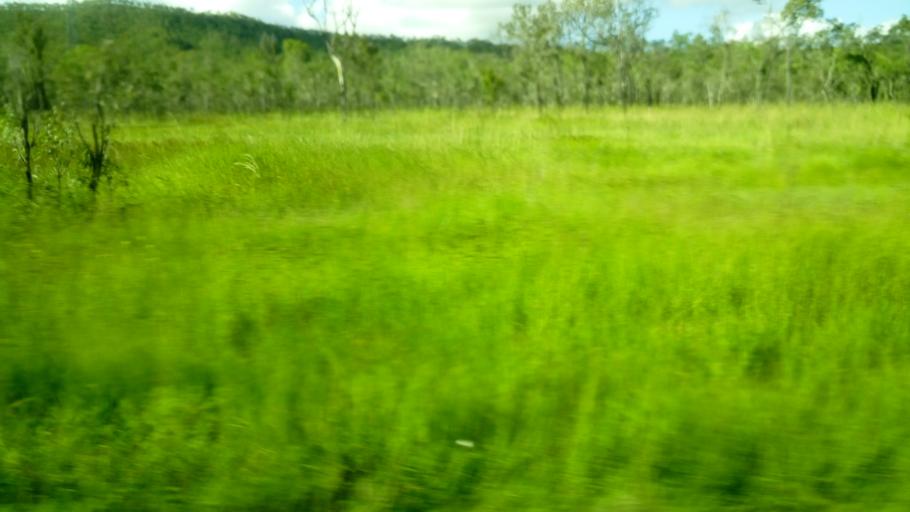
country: AU
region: Queensland
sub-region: Tablelands
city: Mareeba
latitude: -16.7917
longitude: 145.3557
